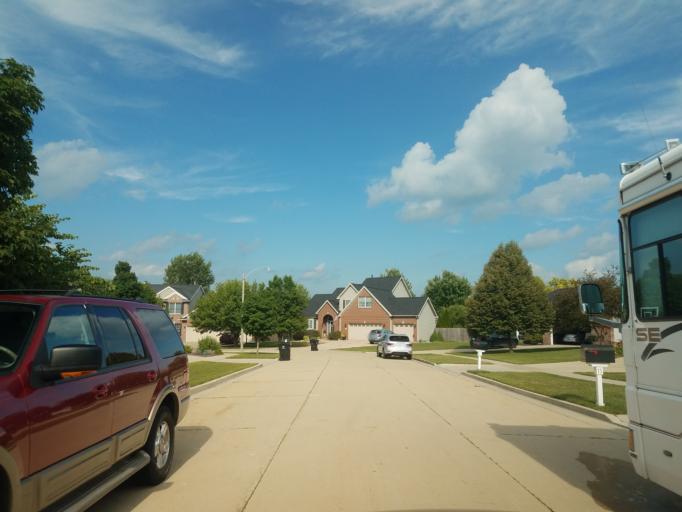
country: US
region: Illinois
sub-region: McLean County
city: Normal
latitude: 40.4984
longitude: -88.9156
